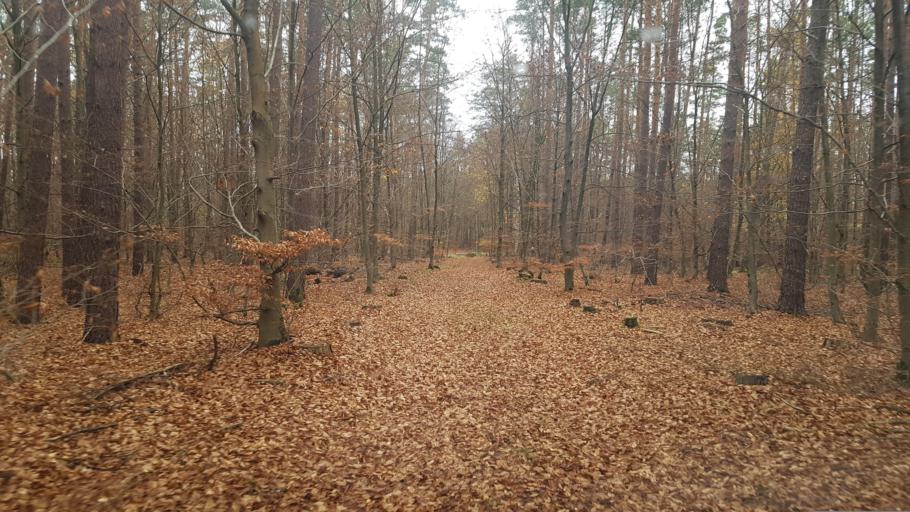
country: DE
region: Brandenburg
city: Wiesenburg
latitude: 52.0810
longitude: 12.4962
